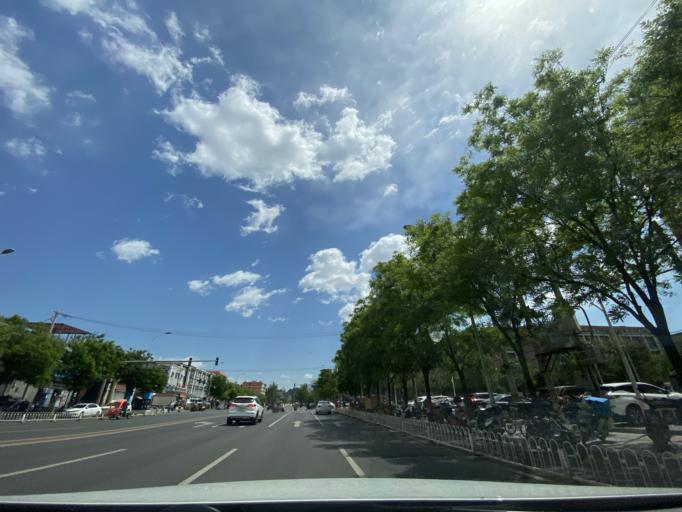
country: CN
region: Beijing
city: Sijiqing
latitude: 39.9279
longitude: 116.2578
